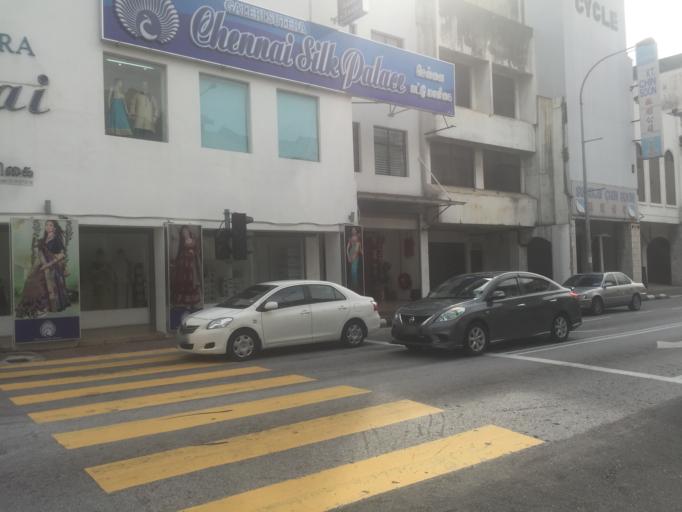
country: MY
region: Perak
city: Ipoh
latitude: 4.5952
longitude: 101.0769
